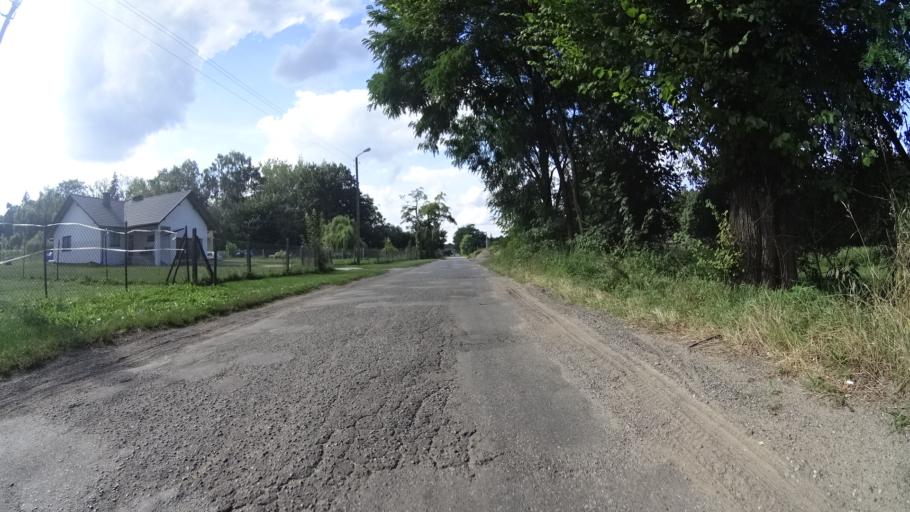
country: PL
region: Masovian Voivodeship
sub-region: Powiat grojecki
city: Mogielnica
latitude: 51.7003
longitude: 20.7123
